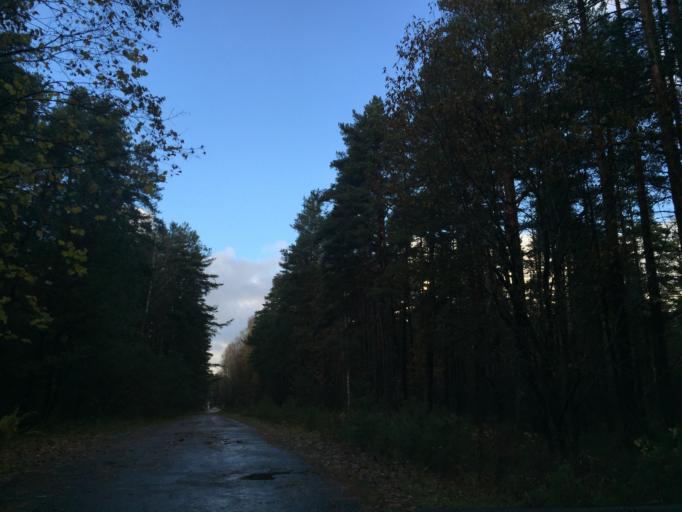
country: LV
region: Riga
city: Bergi
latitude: 57.0161
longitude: 24.3128
